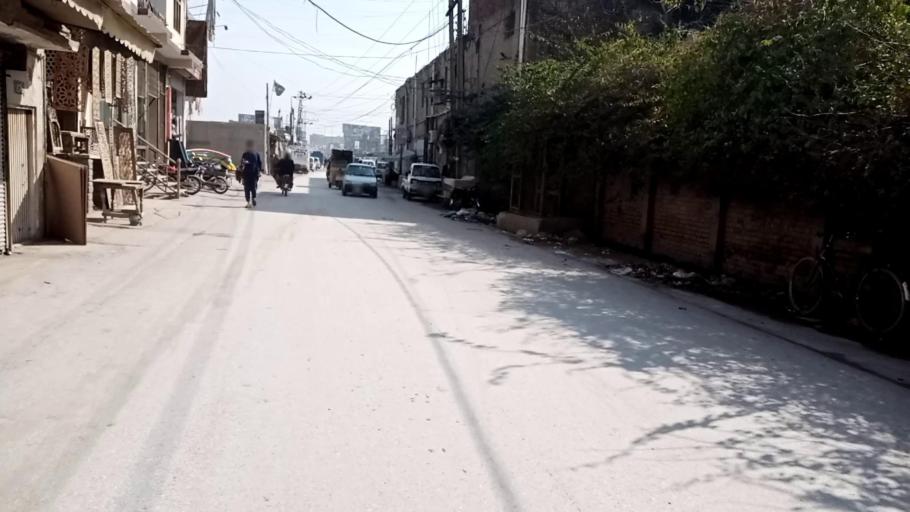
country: PK
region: Khyber Pakhtunkhwa
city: Peshawar
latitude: 34.0094
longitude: 71.5118
